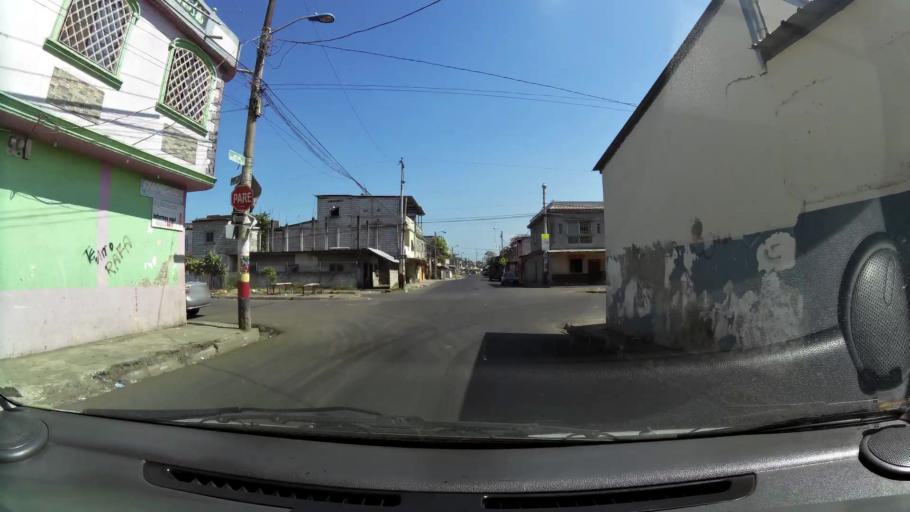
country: EC
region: Guayas
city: Guayaquil
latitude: -2.2302
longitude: -79.9369
